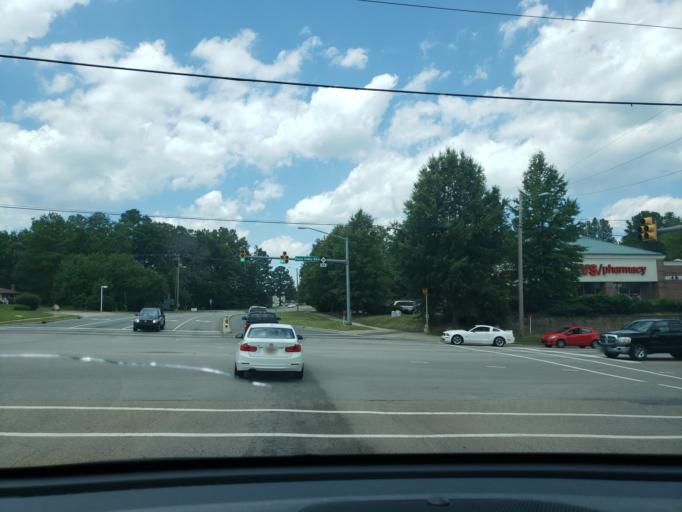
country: US
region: North Carolina
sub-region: Durham County
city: Durham
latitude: 35.9201
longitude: -78.9595
